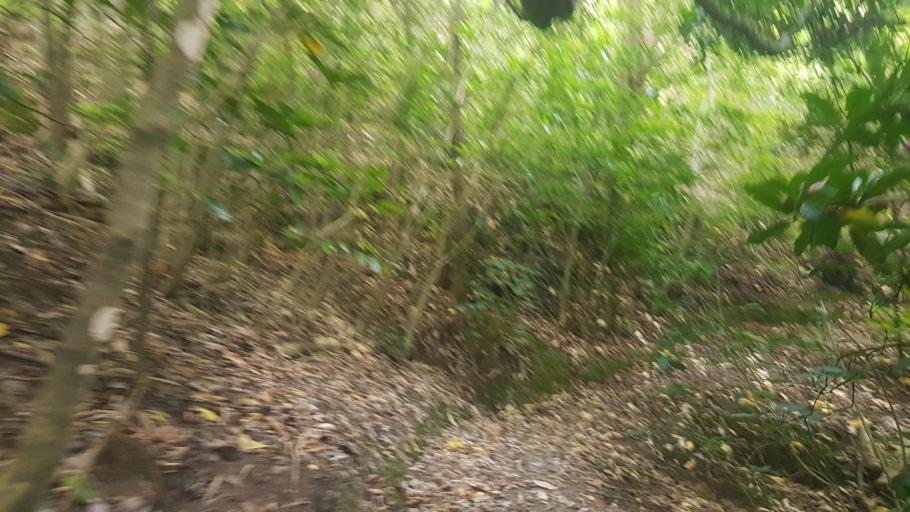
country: NZ
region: Auckland
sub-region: Auckland
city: Pakuranga
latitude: -36.7773
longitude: 175.0013
